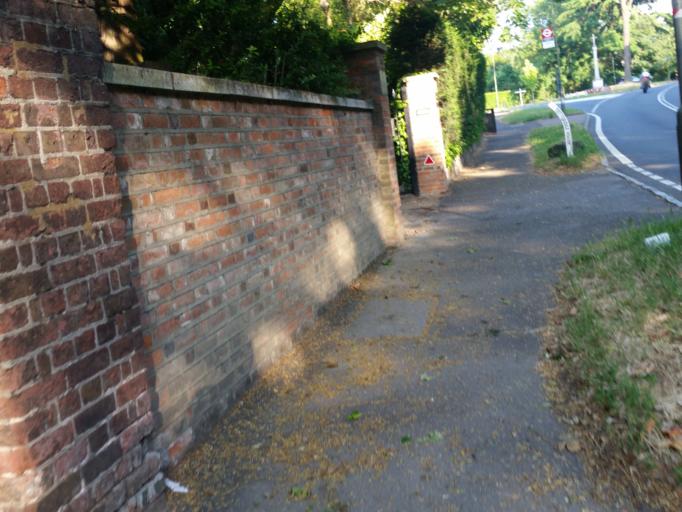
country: GB
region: England
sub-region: Greater London
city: Barnet
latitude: 51.6340
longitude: -0.2018
